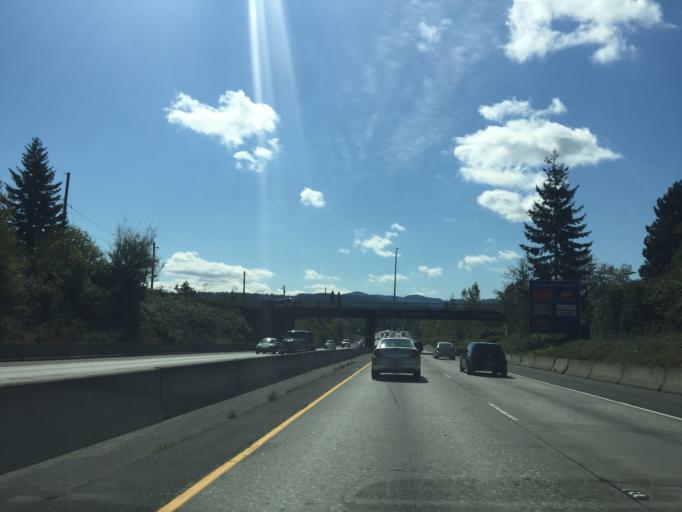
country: US
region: Washington
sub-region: Whatcom County
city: Bellingham
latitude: 48.7639
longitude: -122.4618
